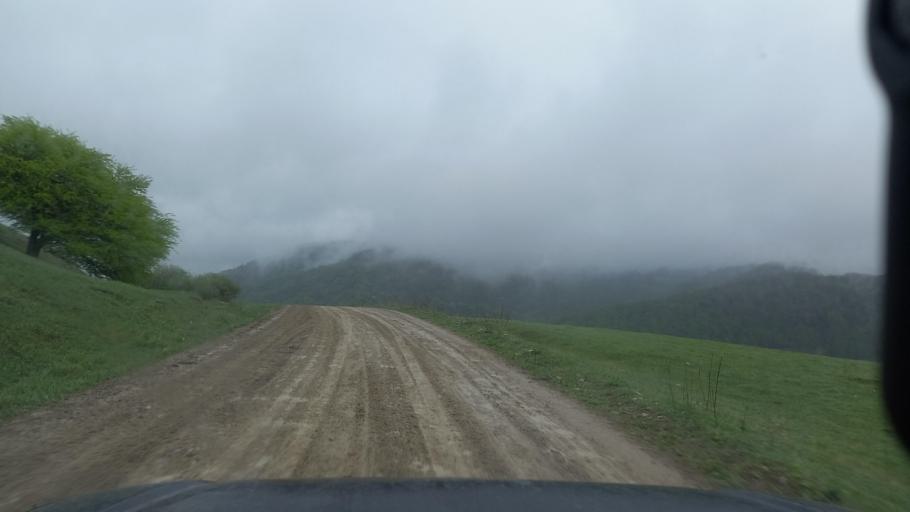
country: RU
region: Kabardino-Balkariya
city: Gundelen
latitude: 43.5940
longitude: 43.1254
